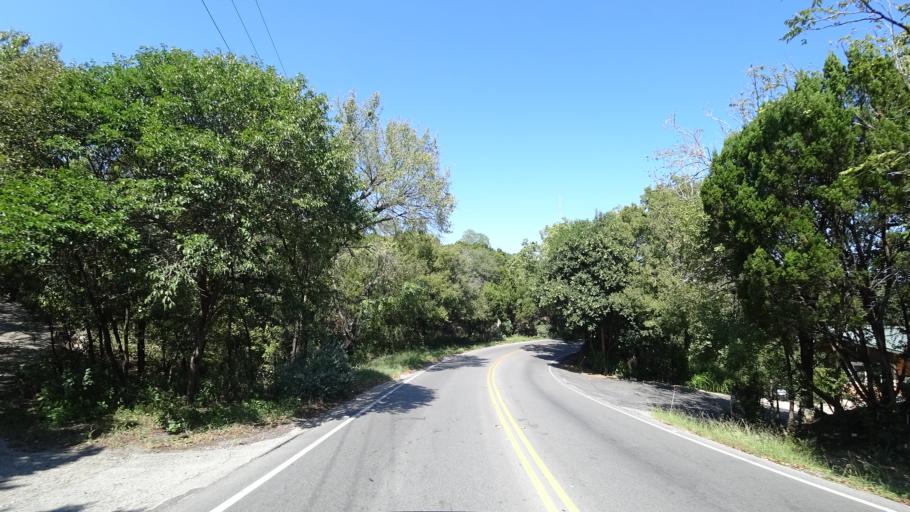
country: US
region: Texas
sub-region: Travis County
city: West Lake Hills
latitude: 30.2973
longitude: -97.7944
